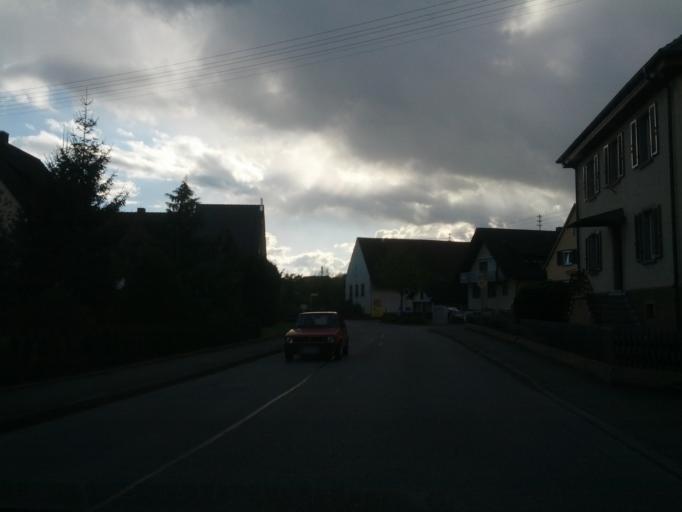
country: DE
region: Baden-Wuerttemberg
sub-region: Freiburg Region
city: Vorstetten
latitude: 48.0717
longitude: 7.8033
